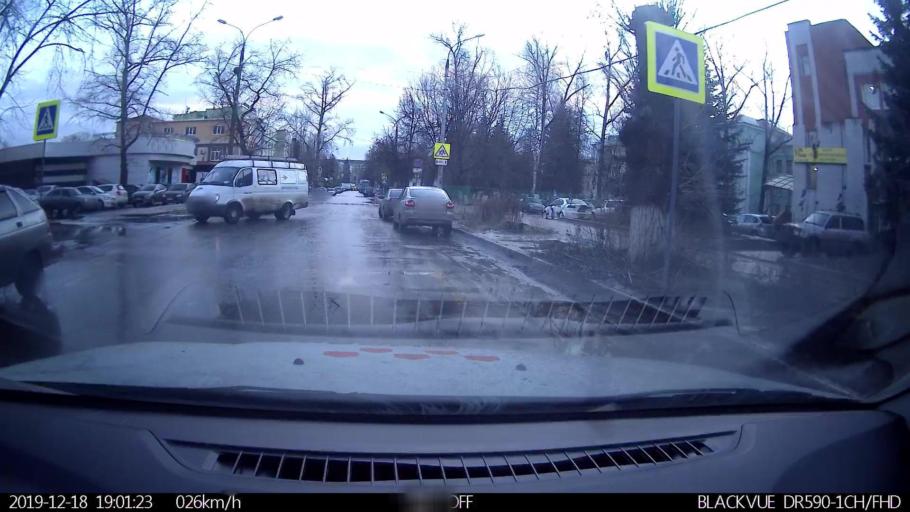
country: RU
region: Nizjnij Novgorod
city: Gorbatovka
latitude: 56.3287
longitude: 43.8541
